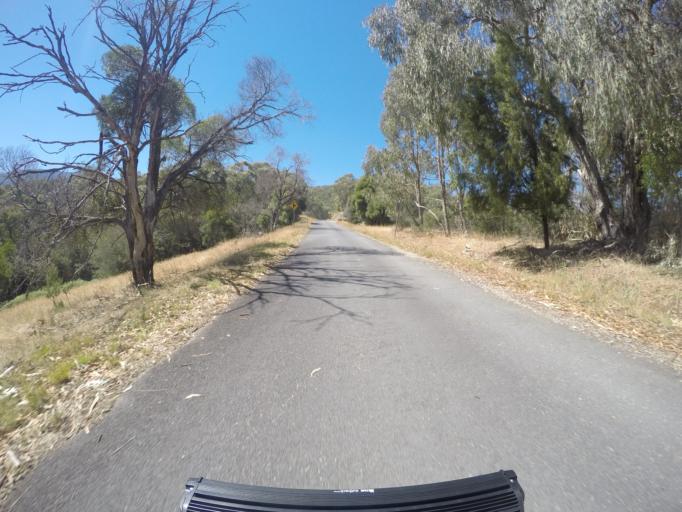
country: AU
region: New South Wales
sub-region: Tumut Shire
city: Tumut
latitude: -35.6214
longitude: 148.2878
